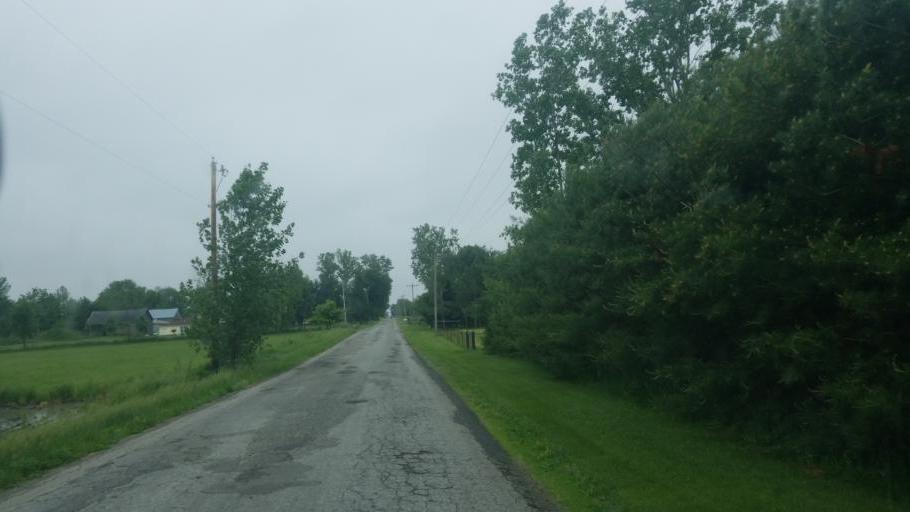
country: US
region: Indiana
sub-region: Marshall County
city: Bremen
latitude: 41.4640
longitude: -86.1176
